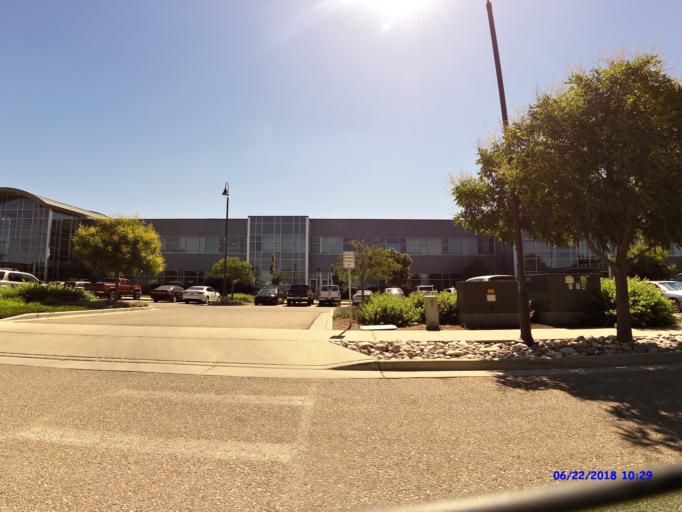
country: US
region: Utah
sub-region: Weber County
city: Riverdale
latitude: 41.1843
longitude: -112.0176
